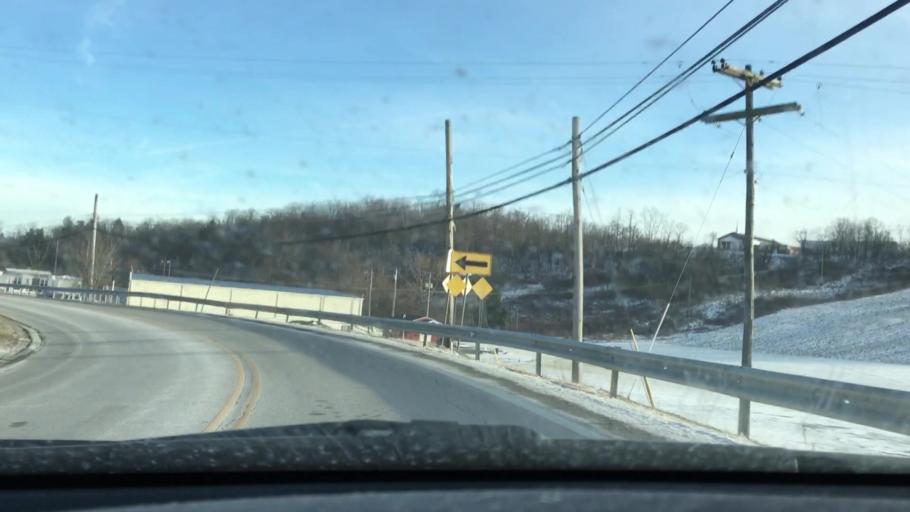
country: US
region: Pennsylvania
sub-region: Washington County
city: Gastonville
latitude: 40.2707
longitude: -80.0196
